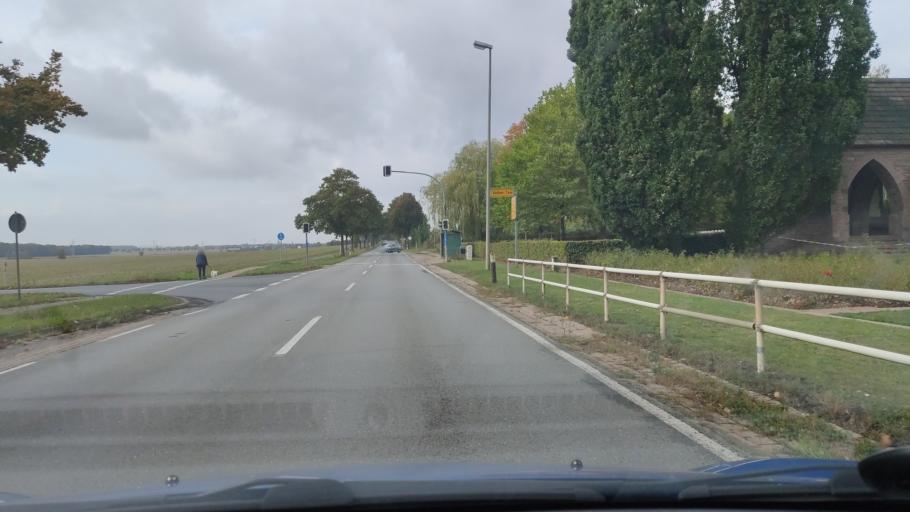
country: DE
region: Lower Saxony
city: Ronnenberg
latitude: 52.3771
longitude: 9.6524
